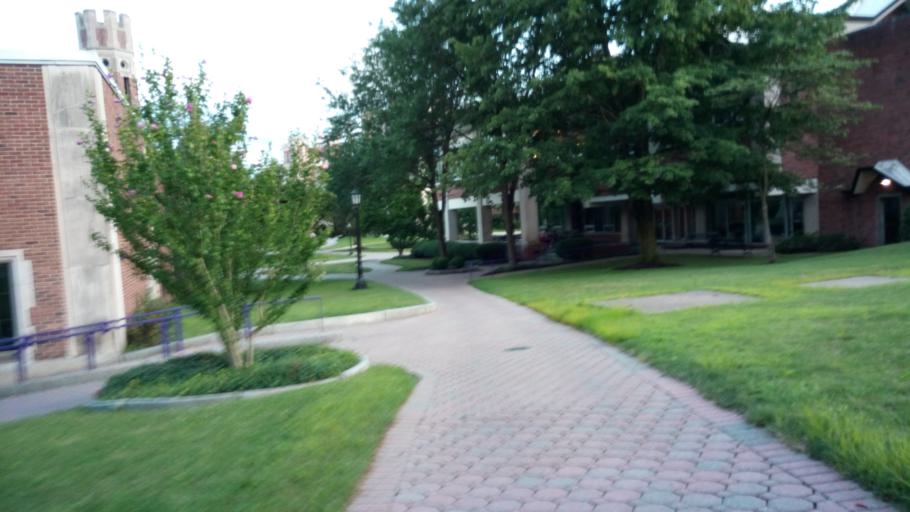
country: US
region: New York
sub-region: Chemung County
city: Elmira
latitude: 42.0970
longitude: -76.8161
